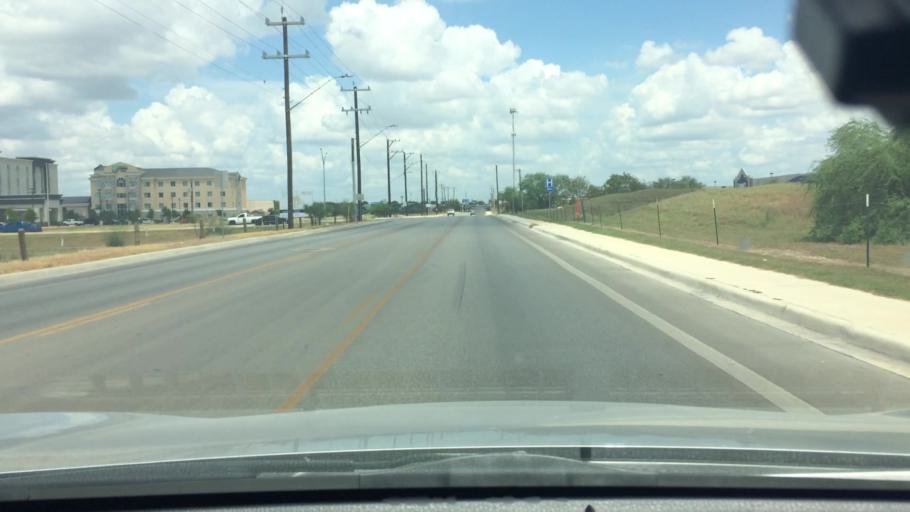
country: US
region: Texas
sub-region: Bexar County
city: China Grove
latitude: 29.3455
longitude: -98.4271
